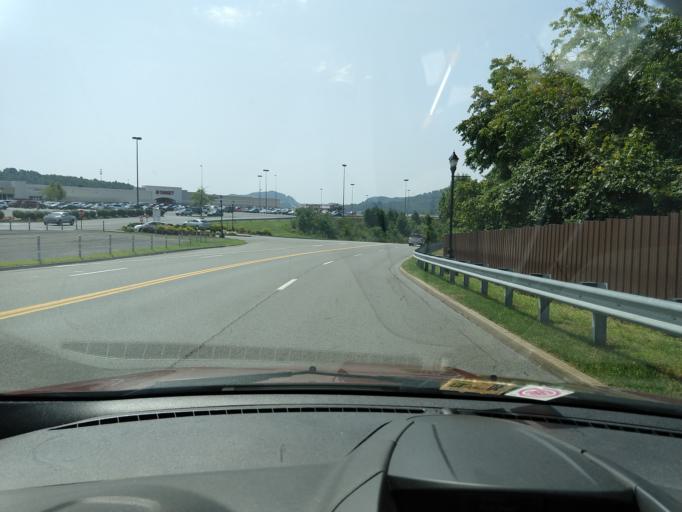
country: US
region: West Virginia
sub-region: Harrison County
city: Bridgeport
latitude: 39.3126
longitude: -80.2767
